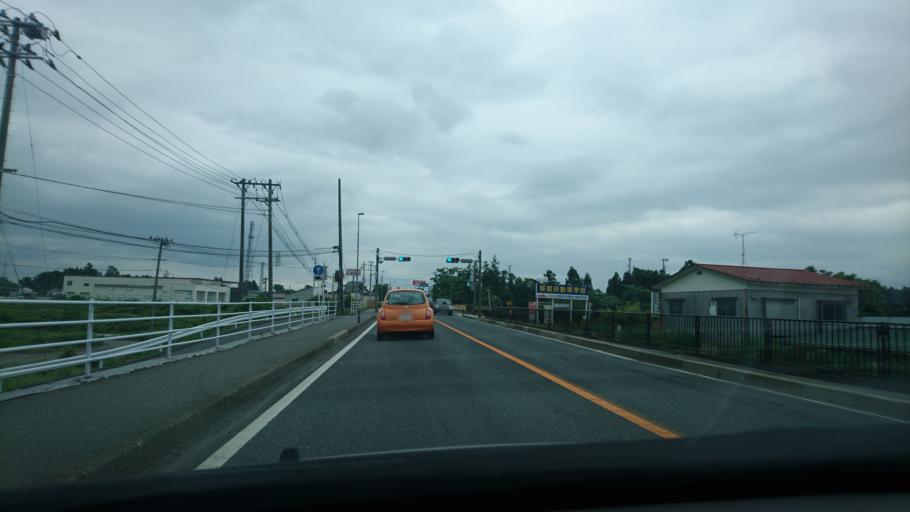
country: JP
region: Miyagi
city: Furukawa
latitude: 38.7418
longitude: 141.0176
